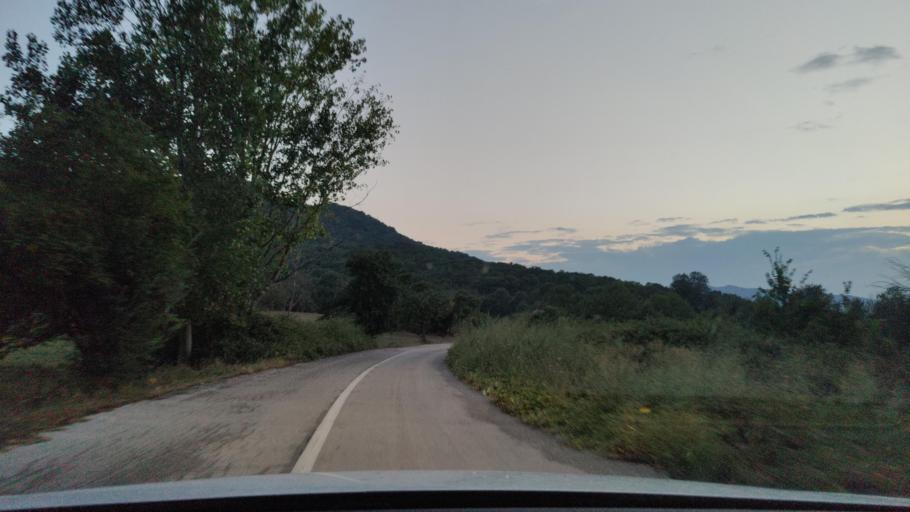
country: GR
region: Central Macedonia
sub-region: Nomos Serron
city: Chrysochorafa
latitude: 41.1795
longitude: 23.1433
